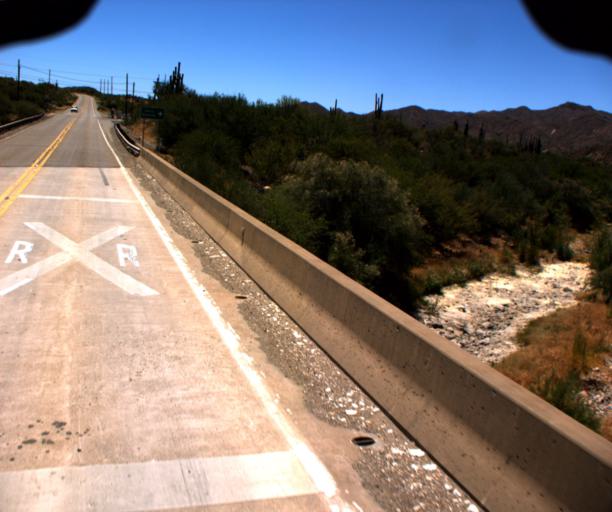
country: US
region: Arizona
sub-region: Pinal County
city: Kearny
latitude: 33.1223
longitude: -110.9763
